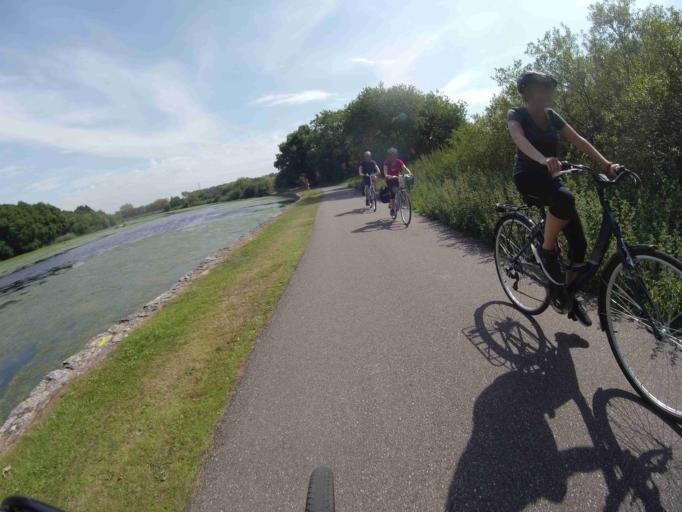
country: GB
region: England
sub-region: Devon
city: Exminster
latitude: 50.6894
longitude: -3.4926
